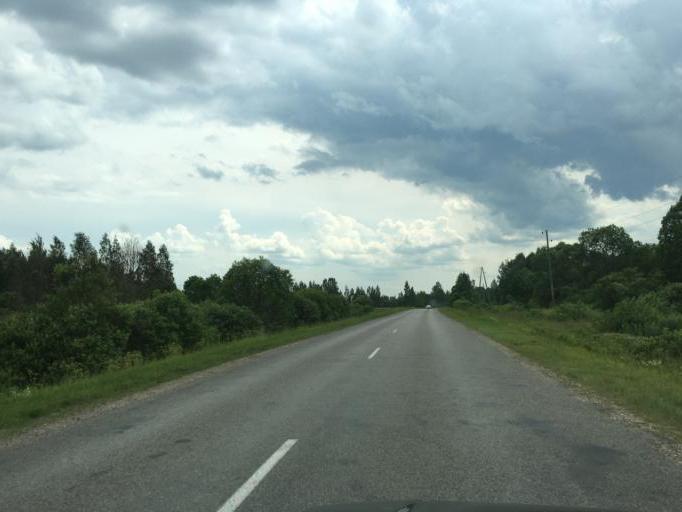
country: LV
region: Rugaju
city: Rugaji
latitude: 56.9442
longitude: 27.0687
